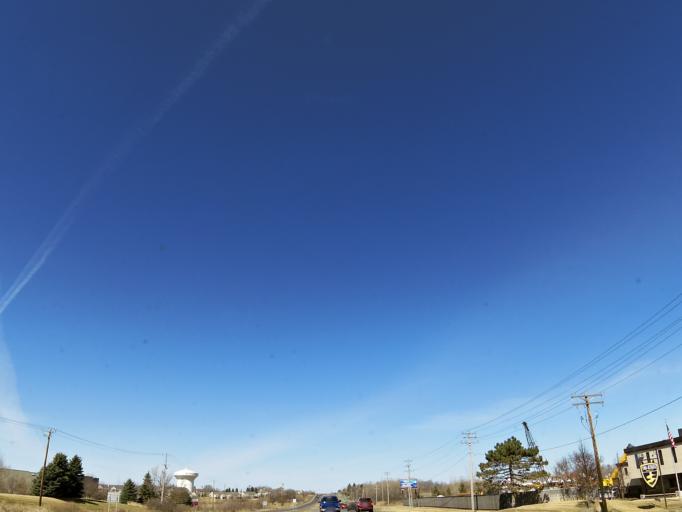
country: US
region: Minnesota
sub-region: Hennepin County
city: Plymouth
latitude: 45.0240
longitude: -93.4954
